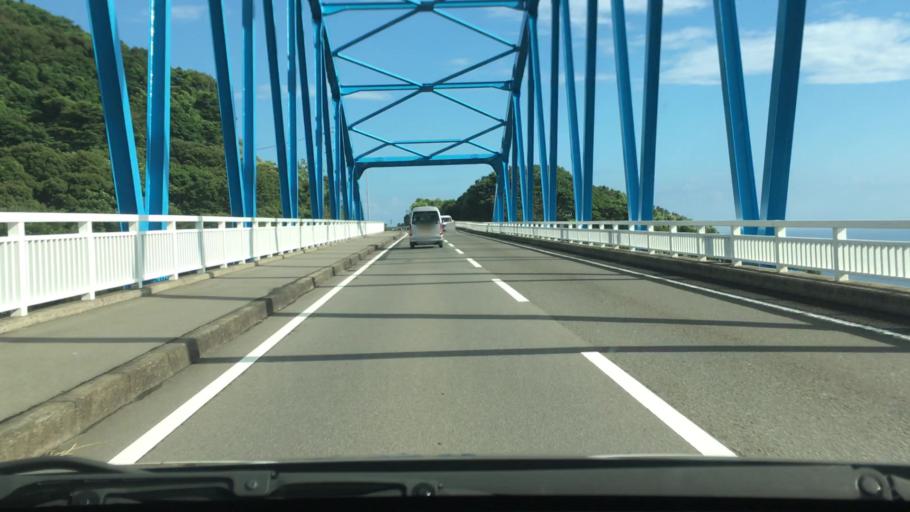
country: JP
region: Nagasaki
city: Togitsu
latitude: 32.8511
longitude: 129.6903
